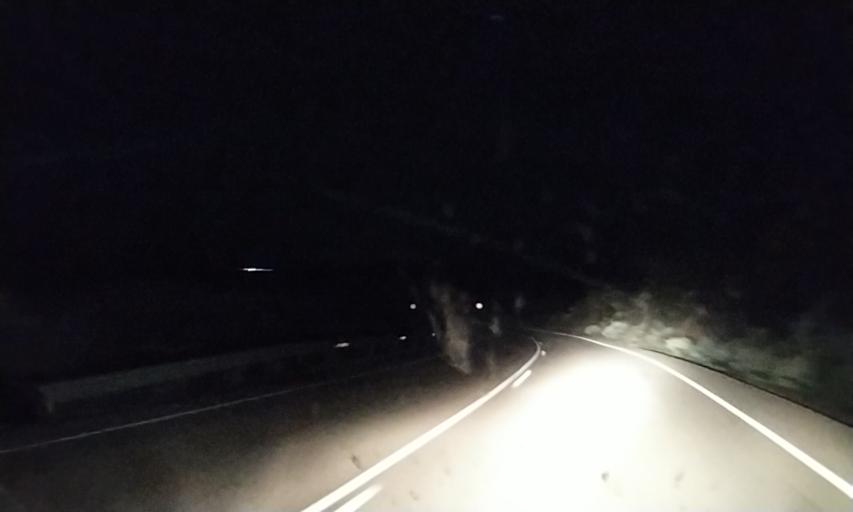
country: ES
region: Castille and Leon
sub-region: Provincia de Salamanca
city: Pastores
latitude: 40.5007
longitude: -6.5764
